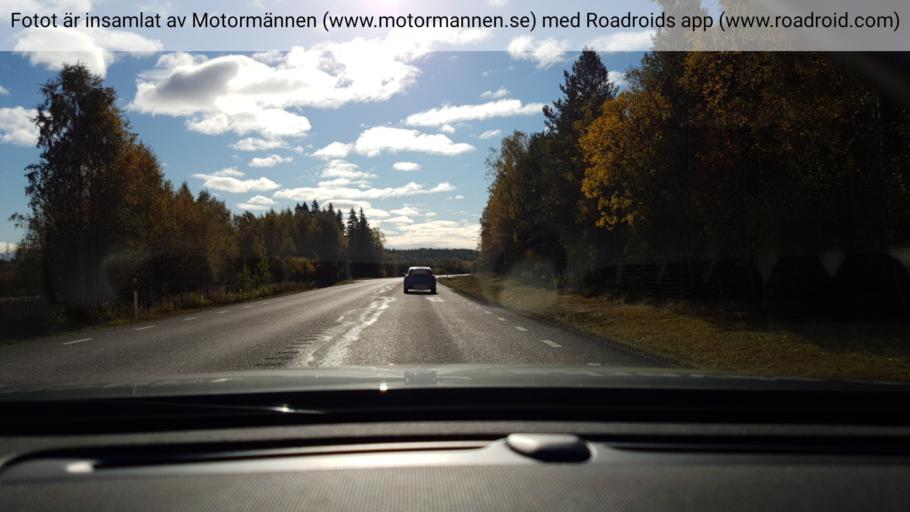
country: SE
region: Vaesterbotten
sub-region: Skelleftea Kommun
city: Burea
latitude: 64.4077
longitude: 21.2978
